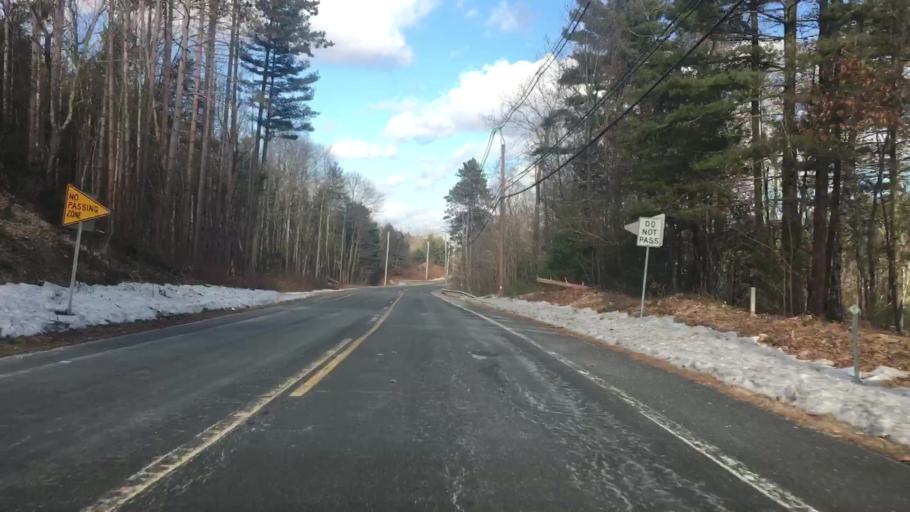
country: US
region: Massachusetts
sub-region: Hampden County
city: Wales
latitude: 42.0893
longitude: -72.2006
